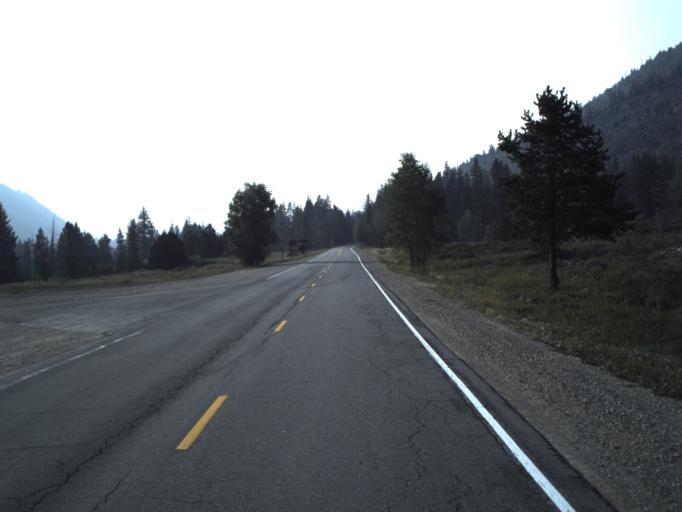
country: US
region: Utah
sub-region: Summit County
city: Francis
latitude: 40.5813
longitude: -111.0480
